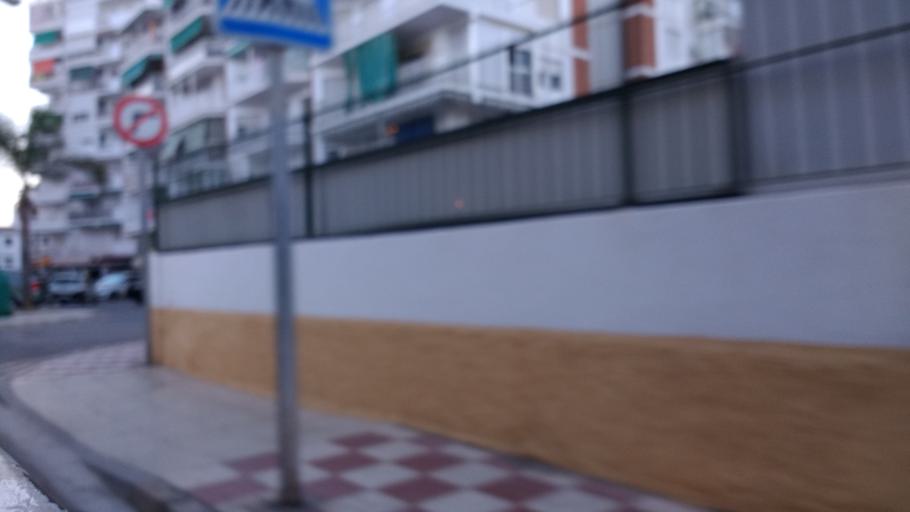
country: ES
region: Andalusia
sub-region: Provincia de Malaga
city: Velez-Malaga
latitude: 36.7433
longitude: -4.0885
